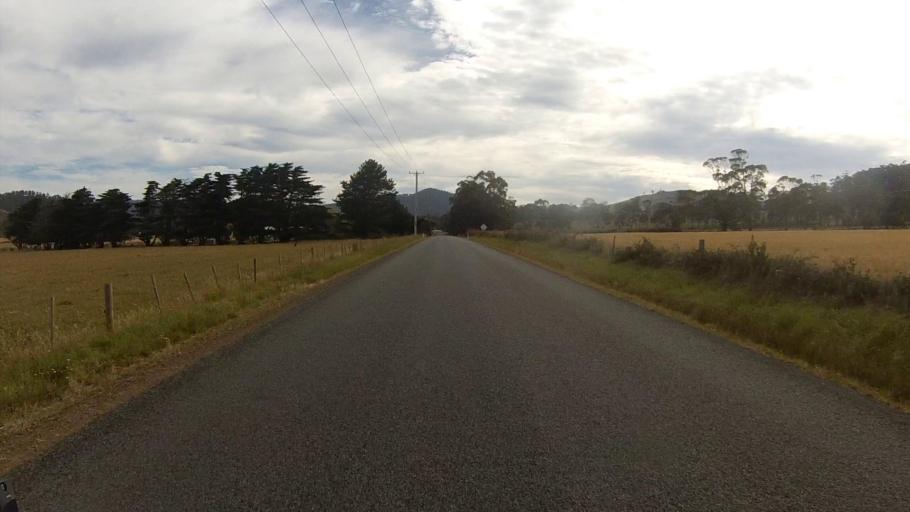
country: AU
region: Tasmania
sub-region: Sorell
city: Sorell
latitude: -42.7945
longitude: 147.7958
